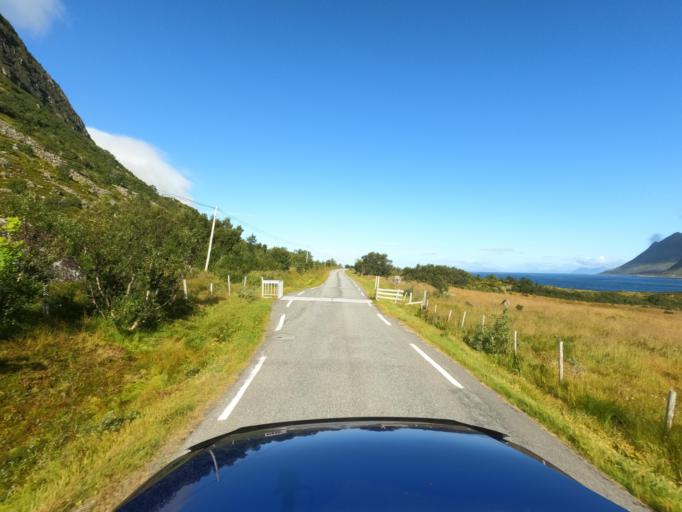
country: NO
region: Nordland
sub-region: Vagan
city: Kabelvag
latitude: 68.2974
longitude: 14.2668
